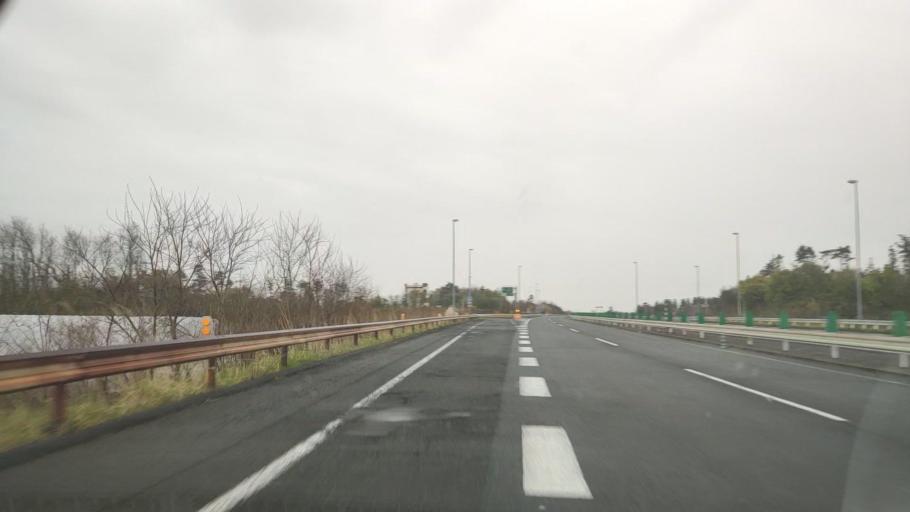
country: JP
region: Akita
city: Noshiromachi
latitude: 40.1215
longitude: 140.0121
